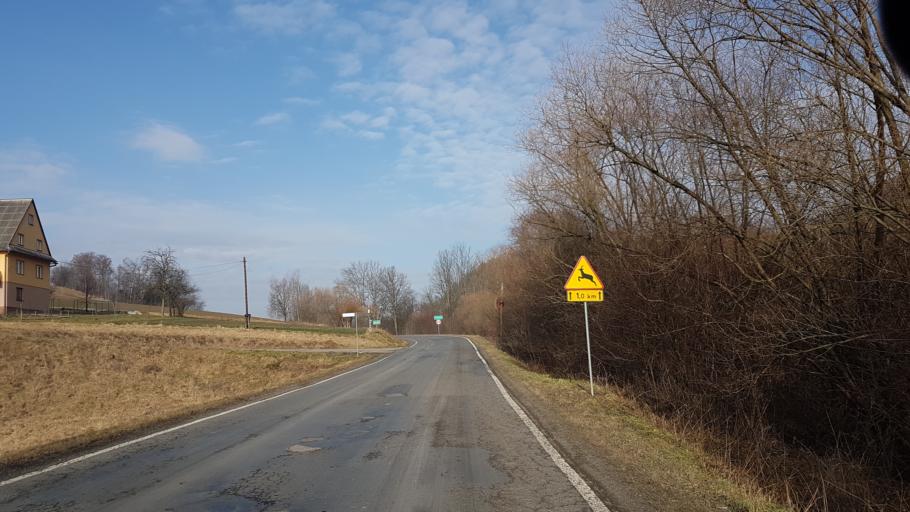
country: PL
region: Lesser Poland Voivodeship
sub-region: Powiat limanowski
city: Lukowica
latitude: 49.6230
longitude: 20.5107
